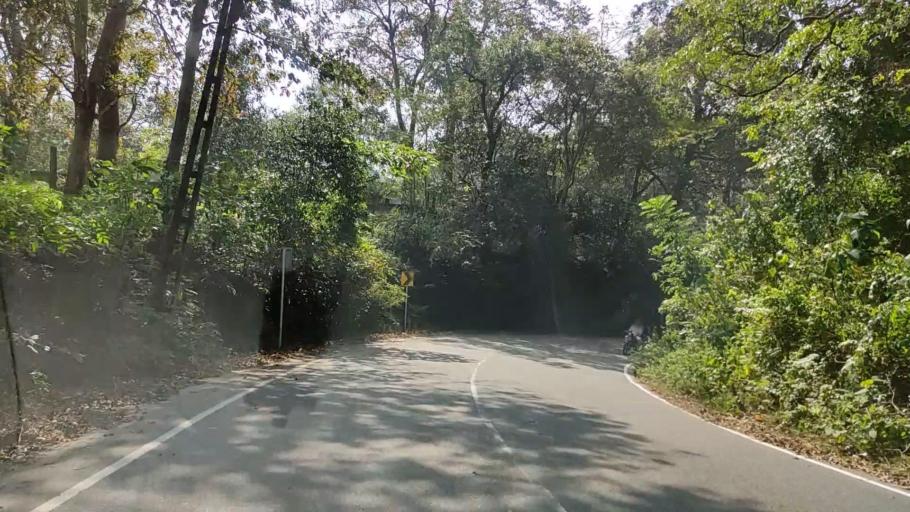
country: IN
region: Kerala
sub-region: Kollam
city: Punalur
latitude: 8.9588
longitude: 77.0675
